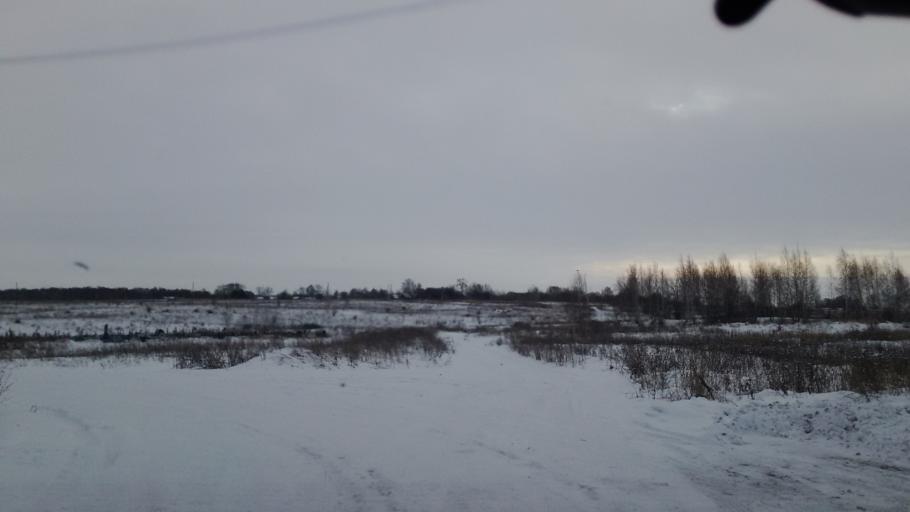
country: RU
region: Tula
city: Bogoroditsk
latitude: 53.7478
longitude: 38.1069
